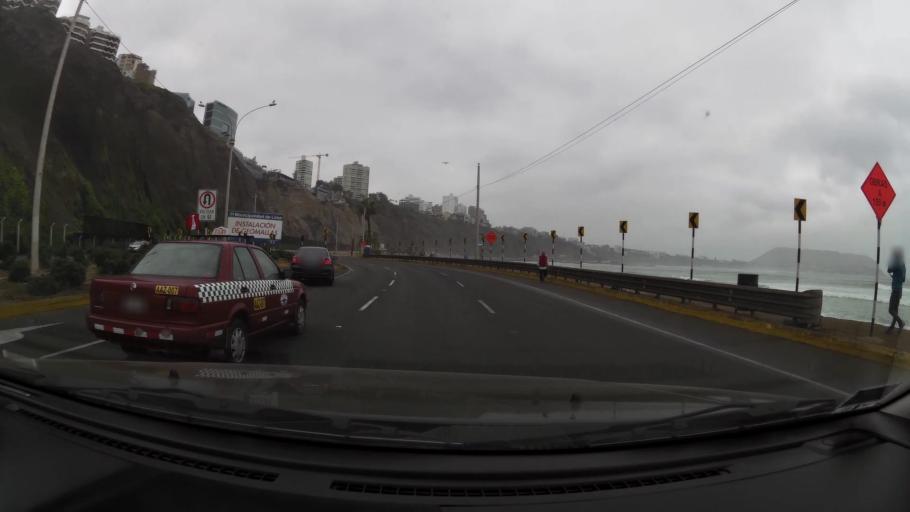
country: PE
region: Lima
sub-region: Lima
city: San Isidro
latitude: -12.1311
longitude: -77.0340
